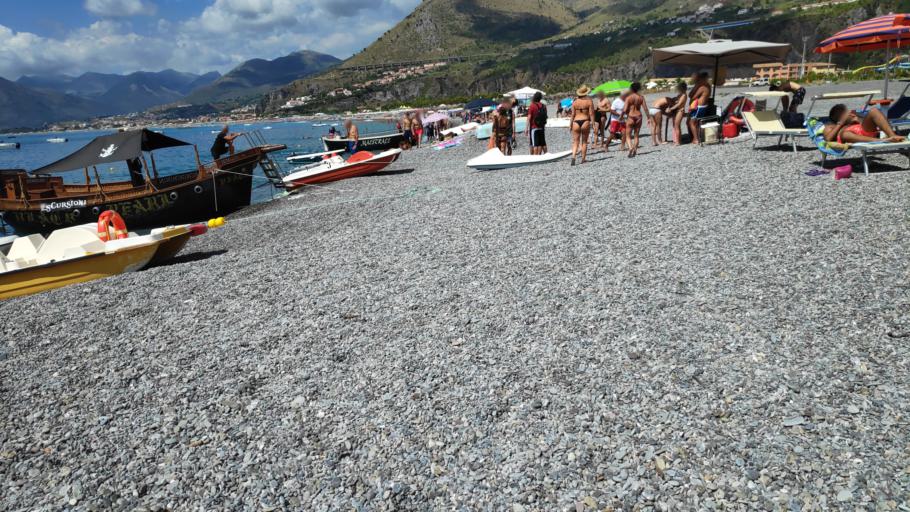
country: IT
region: Calabria
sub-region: Provincia di Cosenza
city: Praia a Mare
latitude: 39.8748
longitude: 15.7830
